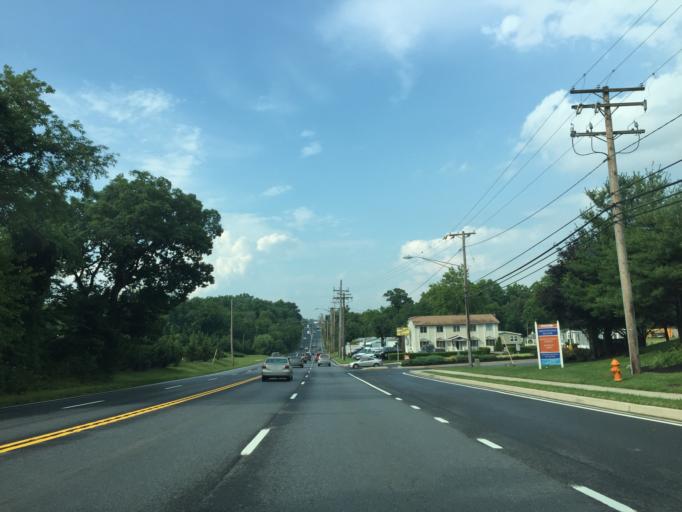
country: US
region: Maryland
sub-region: Anne Arundel County
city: Jessup
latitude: 39.1547
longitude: -76.7992
